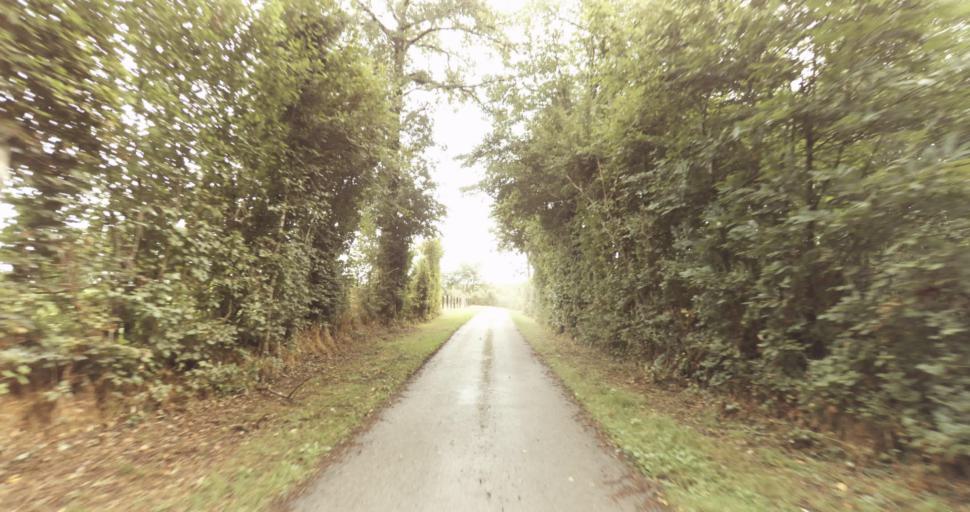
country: FR
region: Lower Normandy
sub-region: Departement de l'Orne
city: Sainte-Gauburge-Sainte-Colombe
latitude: 48.6893
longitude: 0.3293
